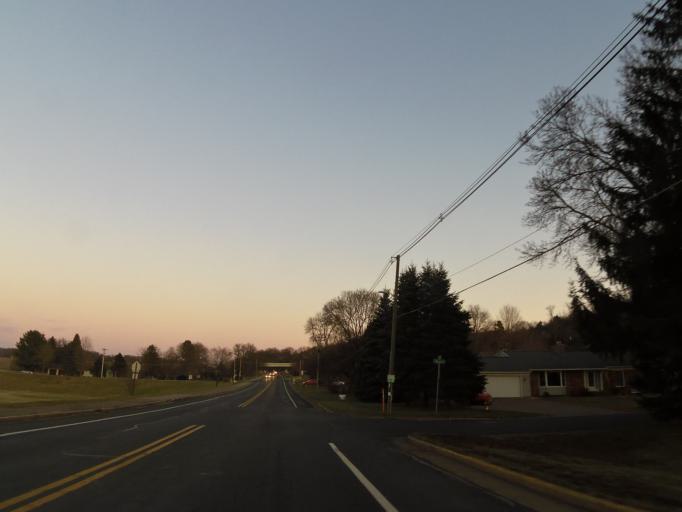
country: US
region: Wisconsin
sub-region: Pierce County
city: River Falls
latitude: 44.8626
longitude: -92.6110
